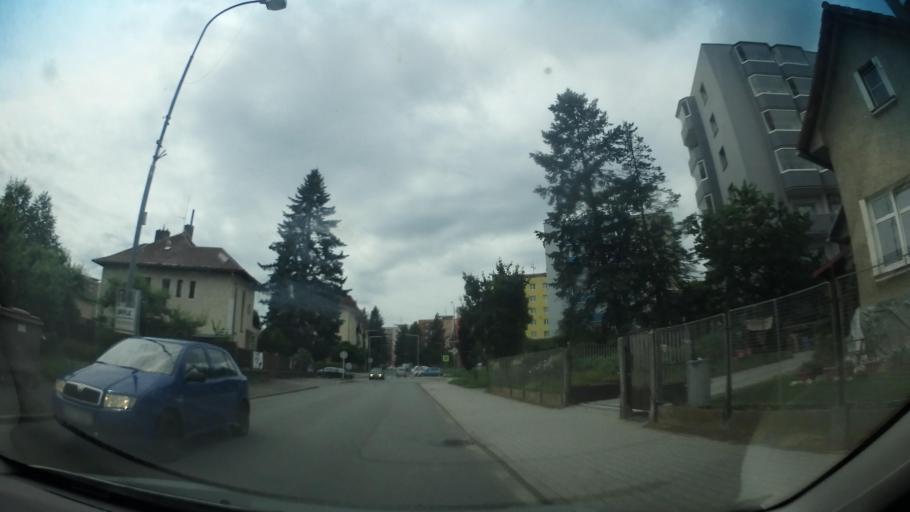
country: CZ
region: Vysocina
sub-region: Okres Zd'ar nad Sazavou
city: Nove Mesto na Morave
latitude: 49.5669
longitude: 16.0769
